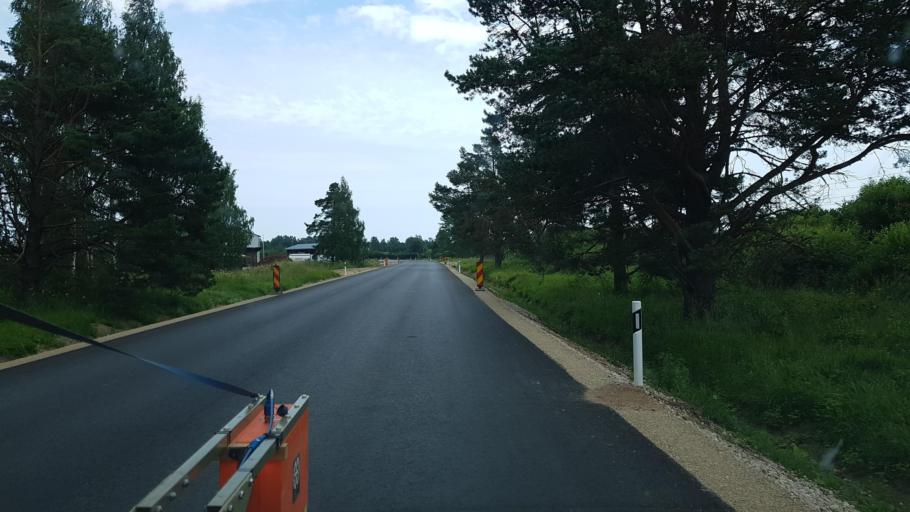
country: EE
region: Polvamaa
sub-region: Raepina vald
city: Rapina
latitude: 58.0884
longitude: 27.4486
